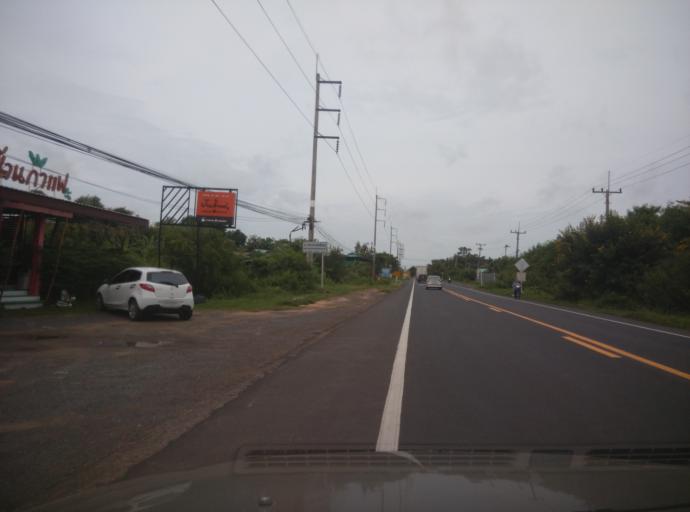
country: TH
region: Sisaket
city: Uthumphon Phisai
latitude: 15.1048
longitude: 104.1297
